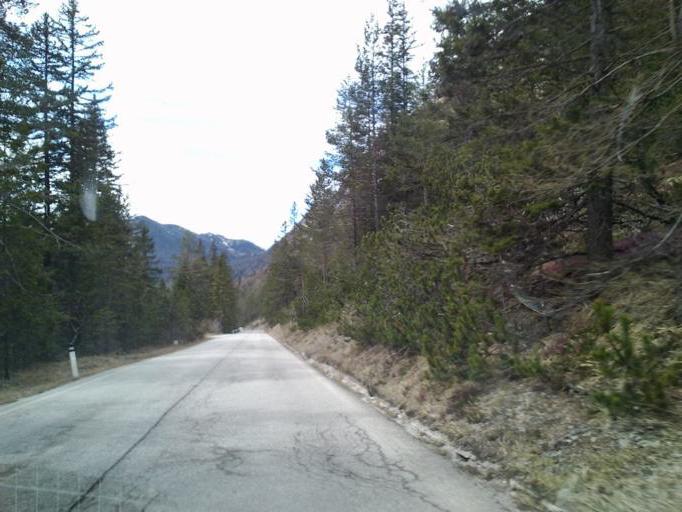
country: IT
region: Veneto
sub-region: Provincia di Belluno
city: Cortina d'Ampezzo
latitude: 46.6068
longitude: 12.2376
